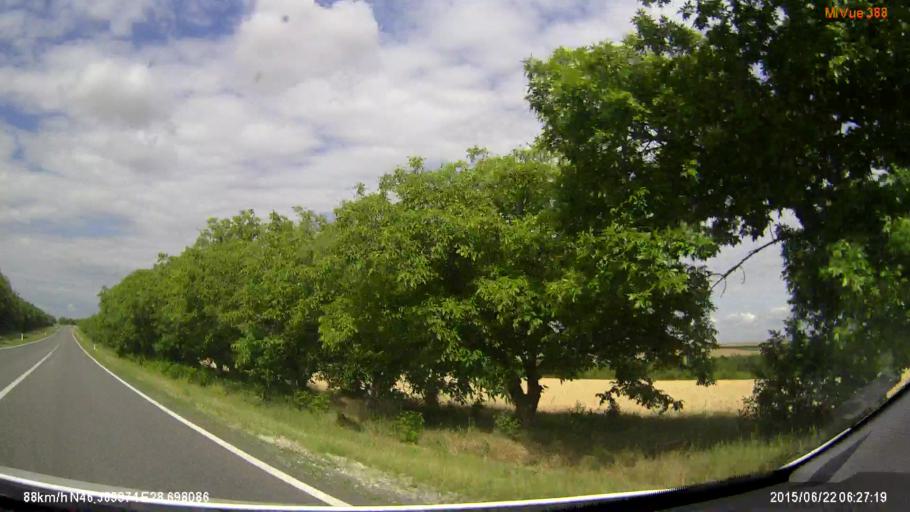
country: MD
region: Gagauzia
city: Bugeac
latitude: 46.3896
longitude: 28.6977
